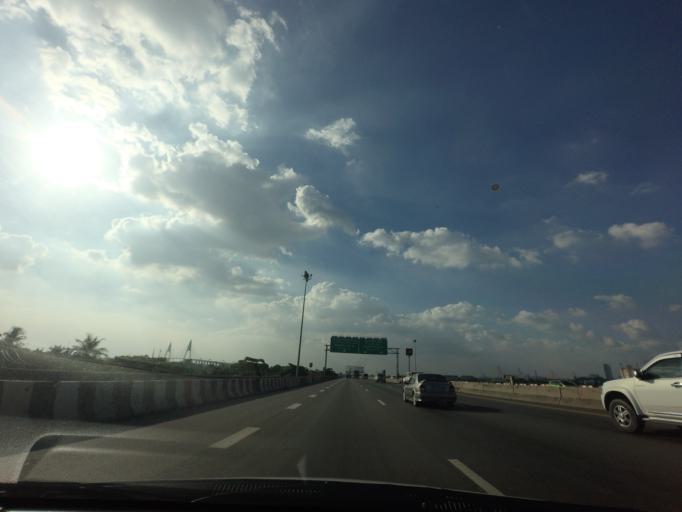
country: TH
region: Samut Prakan
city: Phra Pradaeng
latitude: 13.6369
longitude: 100.5610
